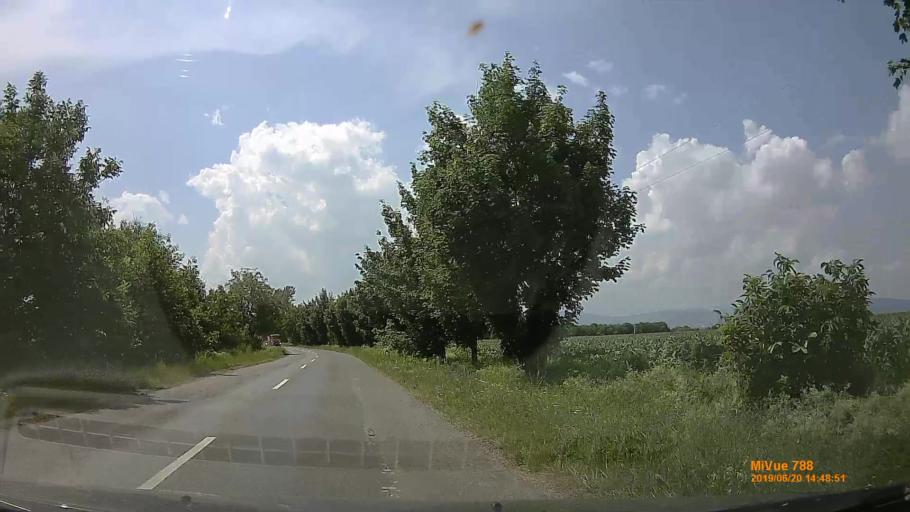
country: HU
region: Baranya
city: Kozarmisleny
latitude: 46.0162
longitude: 18.2826
